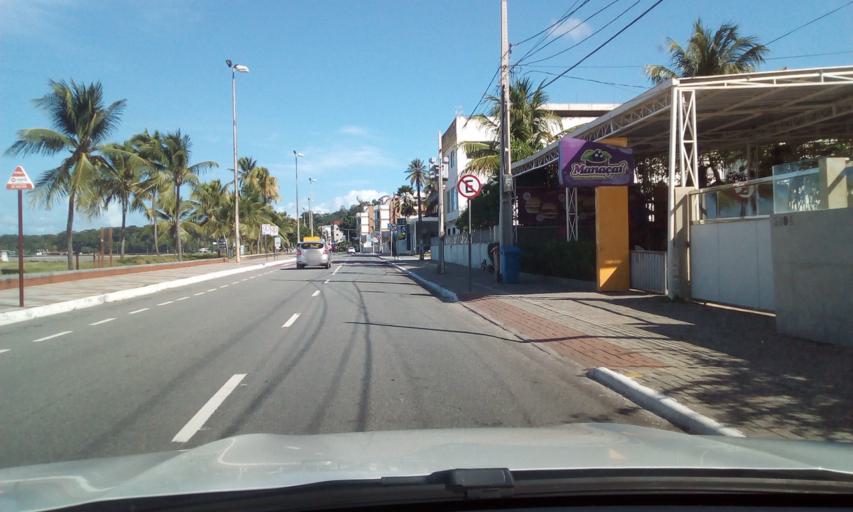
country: BR
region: Paraiba
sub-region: Joao Pessoa
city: Joao Pessoa
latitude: -7.1416
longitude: -34.8152
